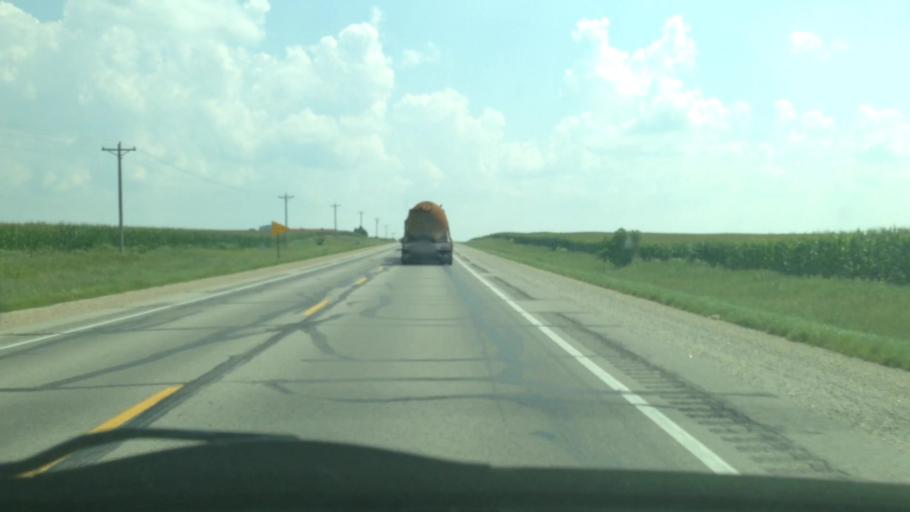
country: US
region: Iowa
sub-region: Chickasaw County
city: New Hampton
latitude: 43.1403
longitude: -92.2988
